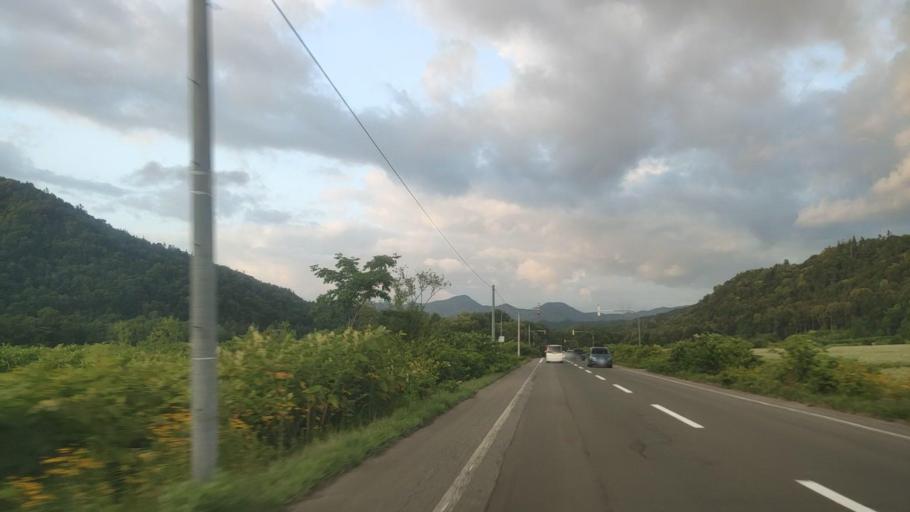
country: JP
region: Hokkaido
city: Ashibetsu
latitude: 43.3062
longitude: 142.1205
